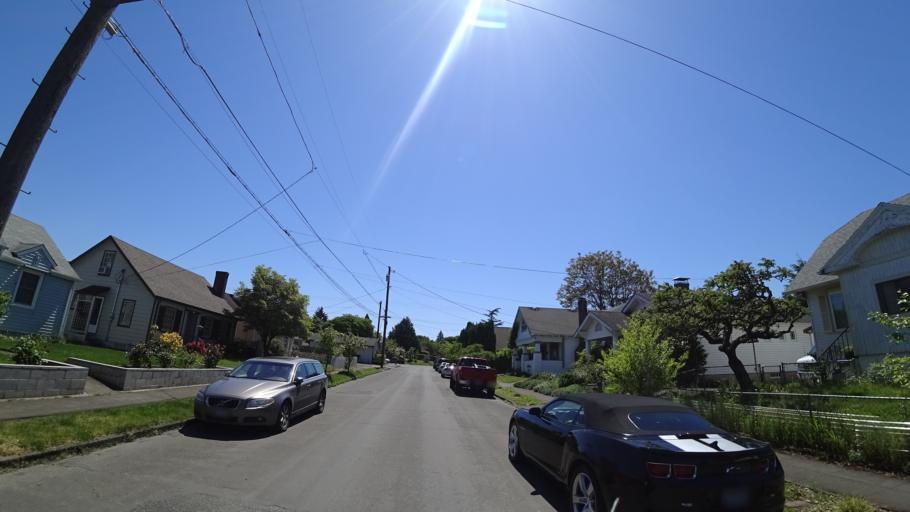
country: US
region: Oregon
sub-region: Multnomah County
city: Lents
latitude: 45.4983
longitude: -122.6041
